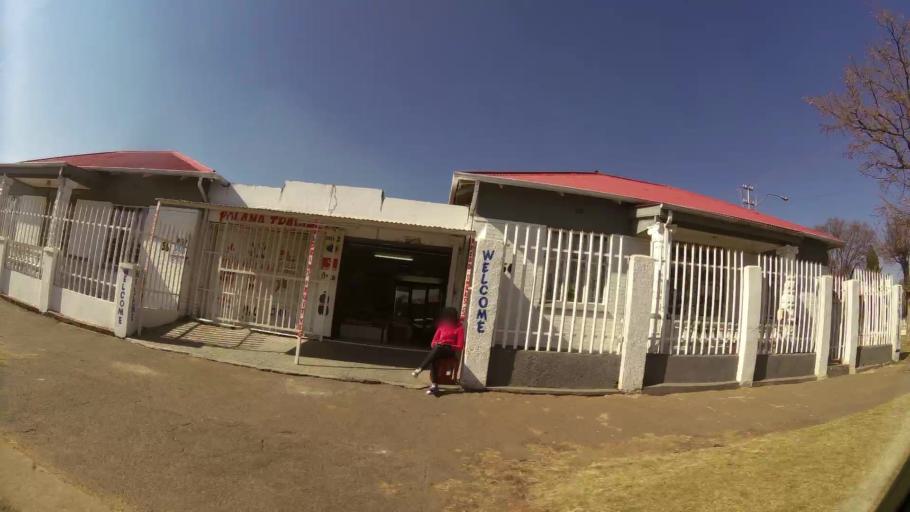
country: ZA
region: Gauteng
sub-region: City of Johannesburg Metropolitan Municipality
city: Johannesburg
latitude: -26.2542
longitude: 28.0392
